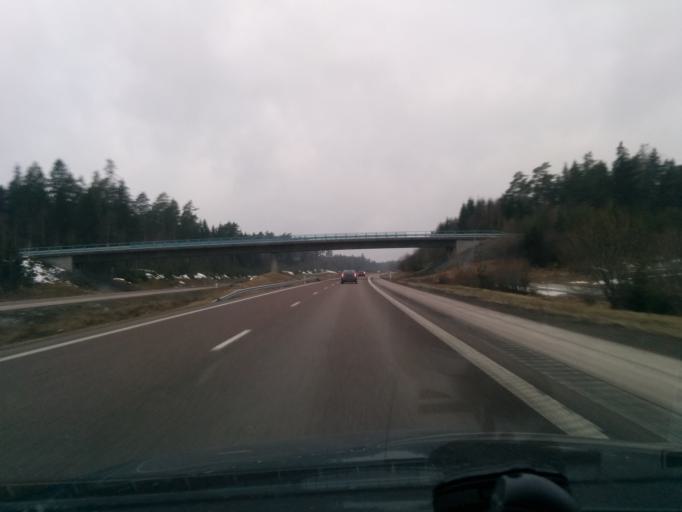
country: SE
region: Uppsala
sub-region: Enkopings Kommun
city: Grillby
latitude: 59.6403
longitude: 17.2256
